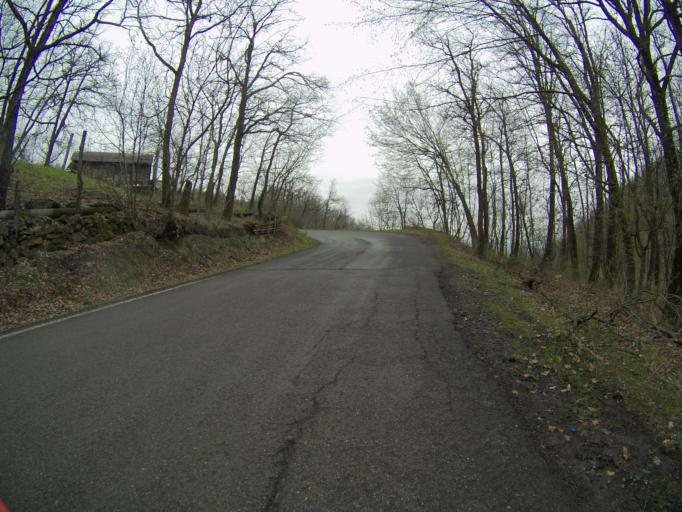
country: IT
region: Emilia-Romagna
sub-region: Provincia di Reggio Emilia
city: Casina
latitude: 44.5421
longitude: 10.4660
